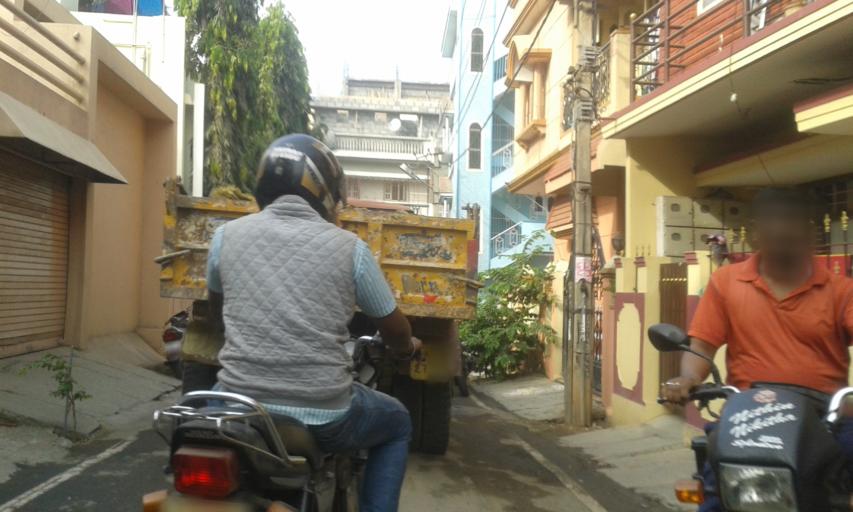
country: IN
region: Karnataka
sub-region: Bangalore Urban
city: Bangalore
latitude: 12.9411
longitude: 77.6083
